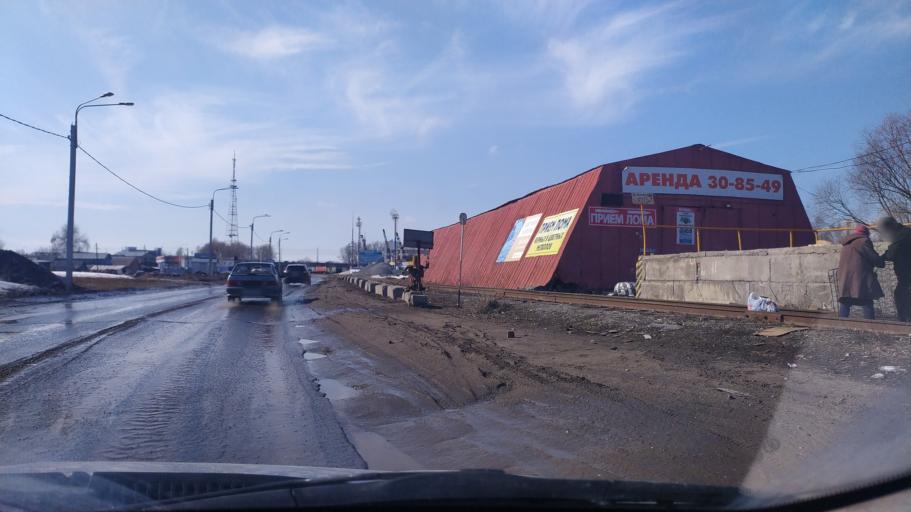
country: RU
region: Chuvashia
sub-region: Cheboksarskiy Rayon
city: Cheboksary
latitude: 56.1174
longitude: 47.2837
